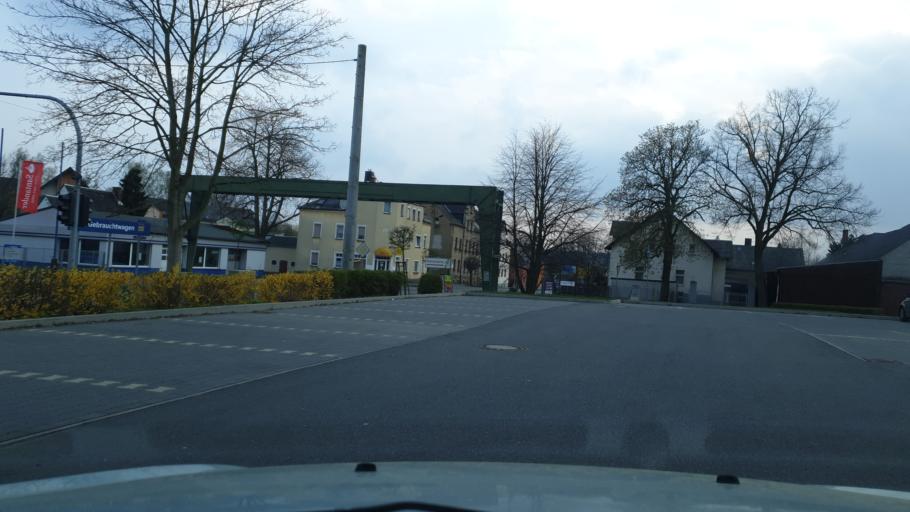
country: DE
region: Saxony
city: Lugau
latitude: 50.7232
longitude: 12.7273
